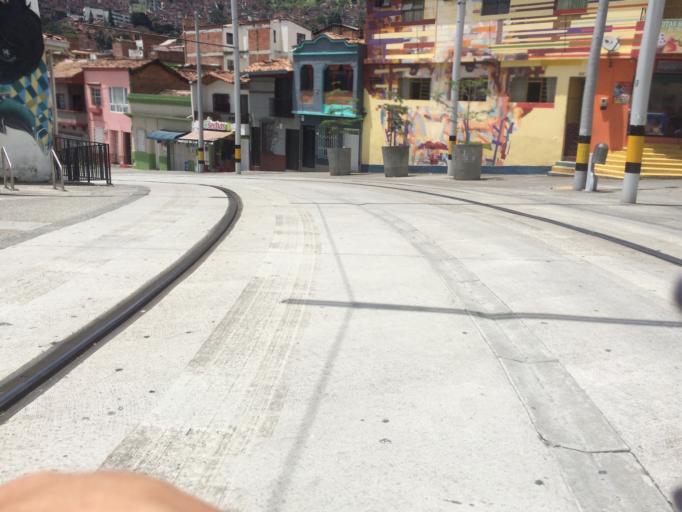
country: CO
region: Antioquia
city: Medellin
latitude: 6.2405
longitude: -75.5522
